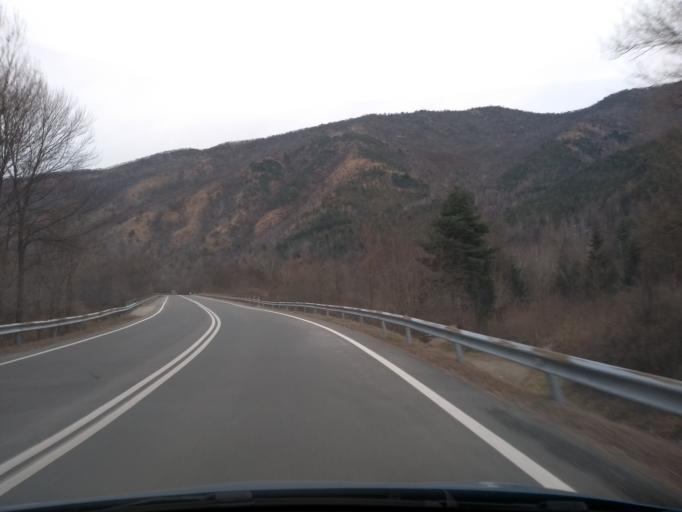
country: IT
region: Piedmont
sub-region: Provincia di Torino
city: Germagnano
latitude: 45.2579
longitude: 7.4600
